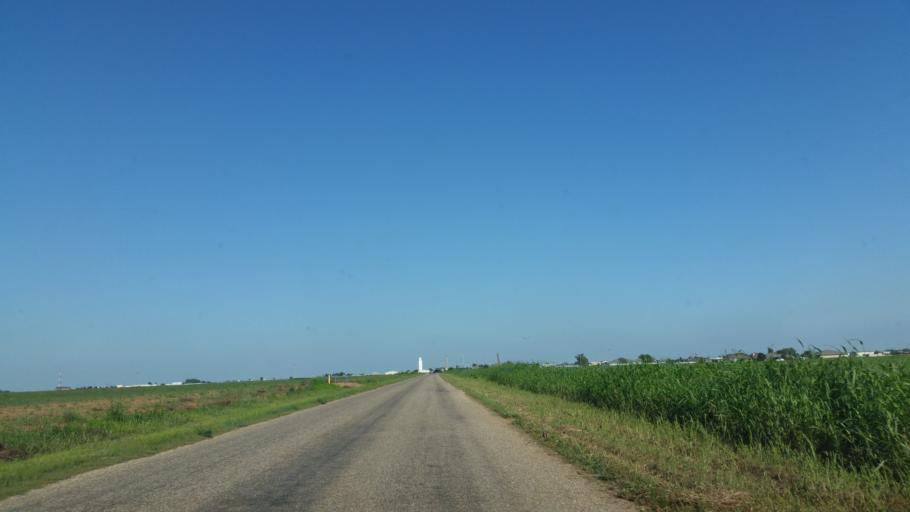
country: US
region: New Mexico
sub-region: Curry County
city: Clovis
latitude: 34.4630
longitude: -103.2187
